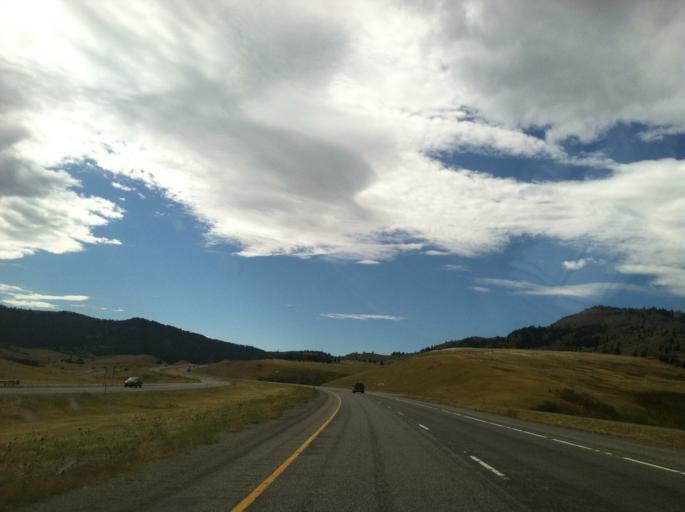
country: US
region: Montana
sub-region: Park County
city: Livingston
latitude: 45.6622
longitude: -110.7423
